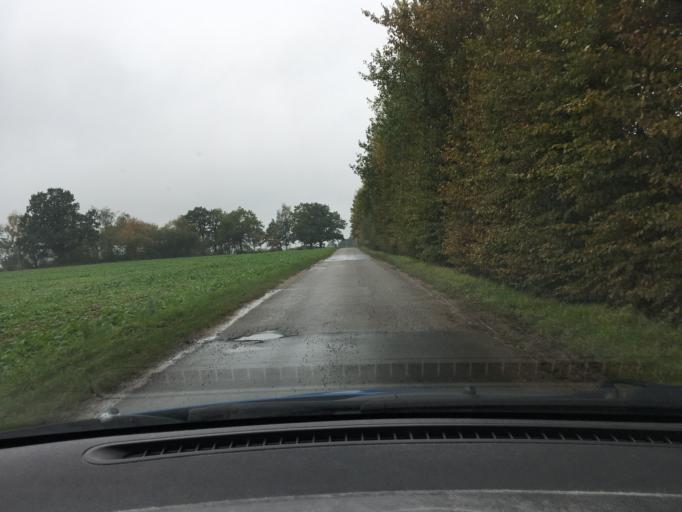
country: DE
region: Schleswig-Holstein
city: Bosau
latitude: 54.0974
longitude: 10.4629
